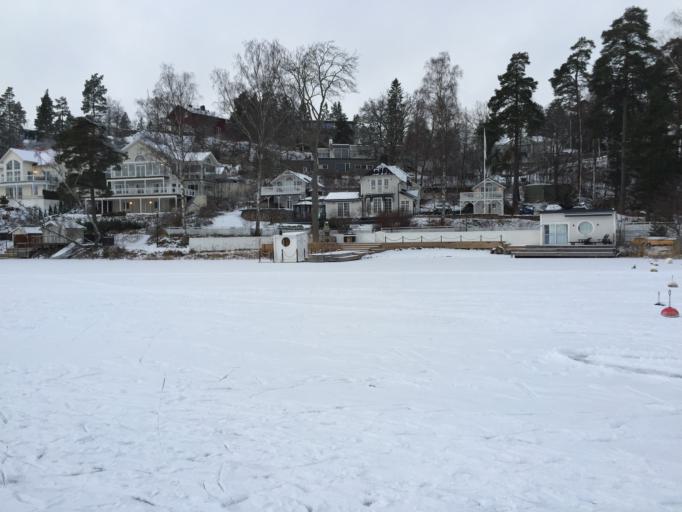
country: SE
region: Stockholm
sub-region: Salems Kommun
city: Ronninge
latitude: 59.1856
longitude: 17.7566
